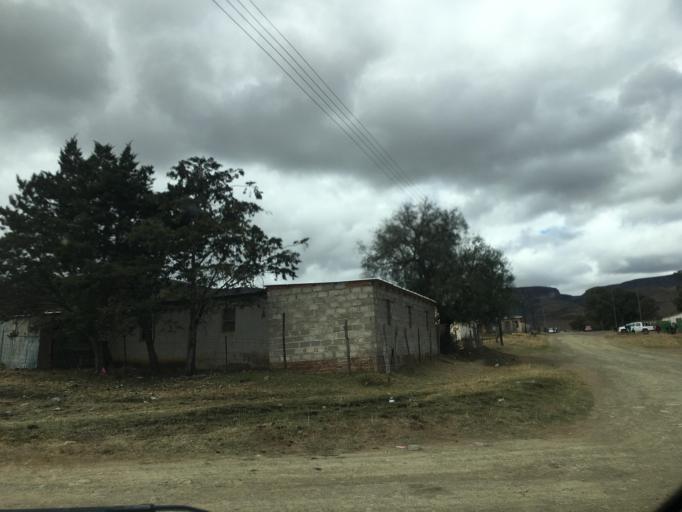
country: ZA
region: Eastern Cape
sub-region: Chris Hani District Municipality
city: Cala
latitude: -31.5247
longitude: 27.6899
